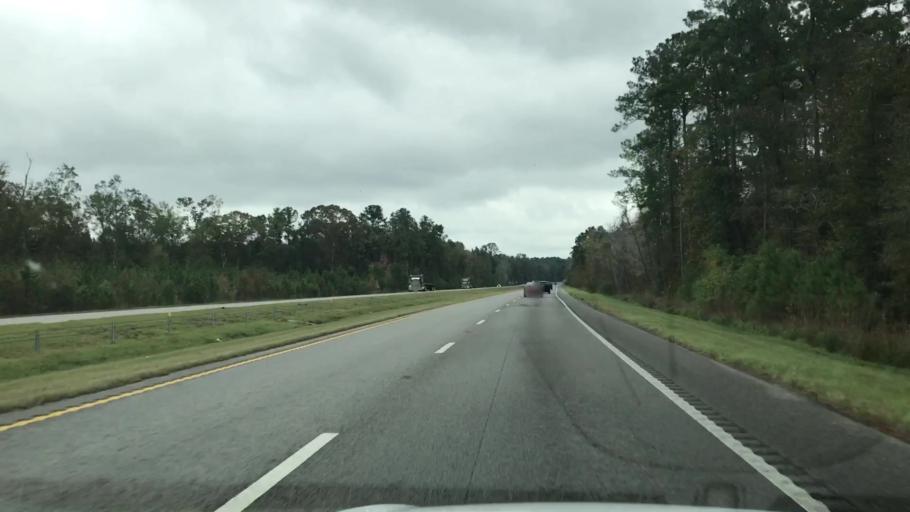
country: US
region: South Carolina
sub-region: Colleton County
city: Walterboro
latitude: 32.7206
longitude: -80.6029
